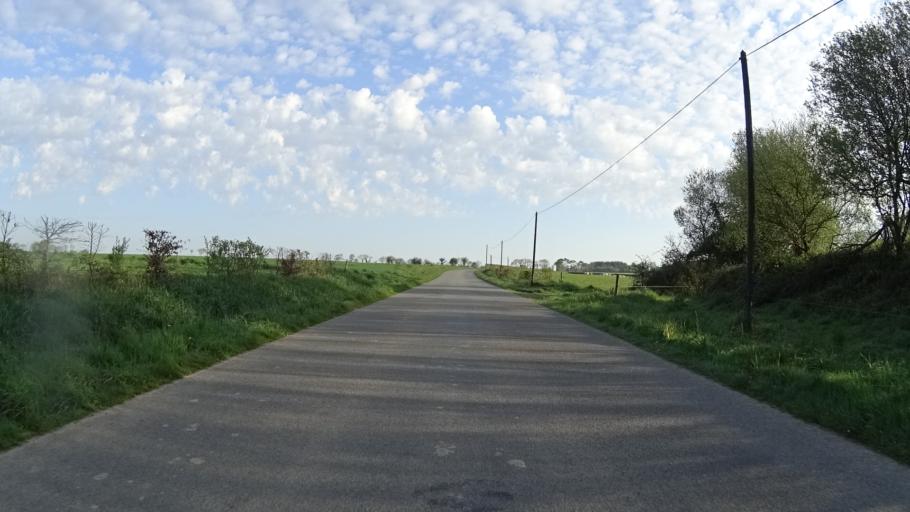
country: FR
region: Brittany
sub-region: Departement du Finistere
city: Sizun
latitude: 48.4207
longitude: -4.0747
